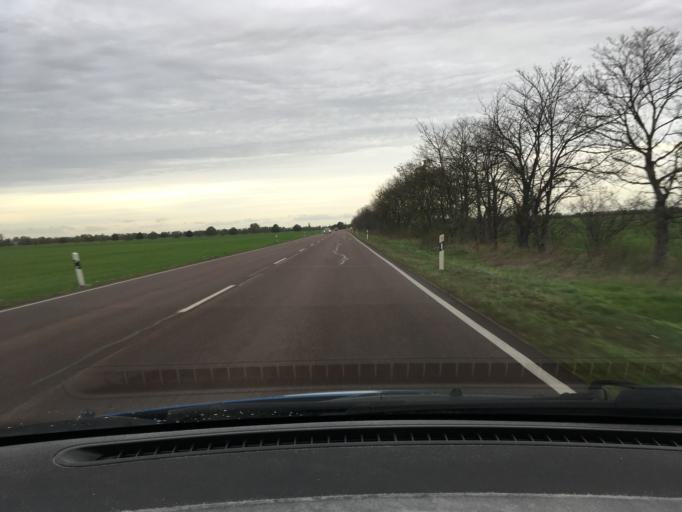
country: DE
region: Saxony-Anhalt
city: Zerbst
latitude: 51.9838
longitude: 12.0536
